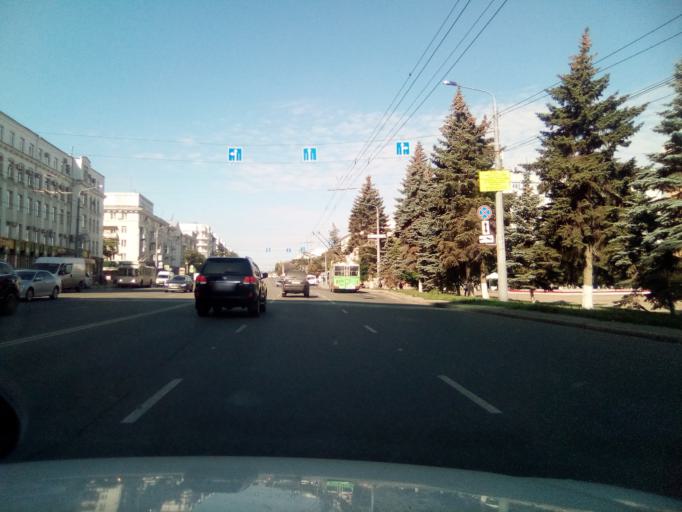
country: RU
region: Chelyabinsk
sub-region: Gorod Chelyabinsk
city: Chelyabinsk
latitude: 55.1601
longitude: 61.3980
